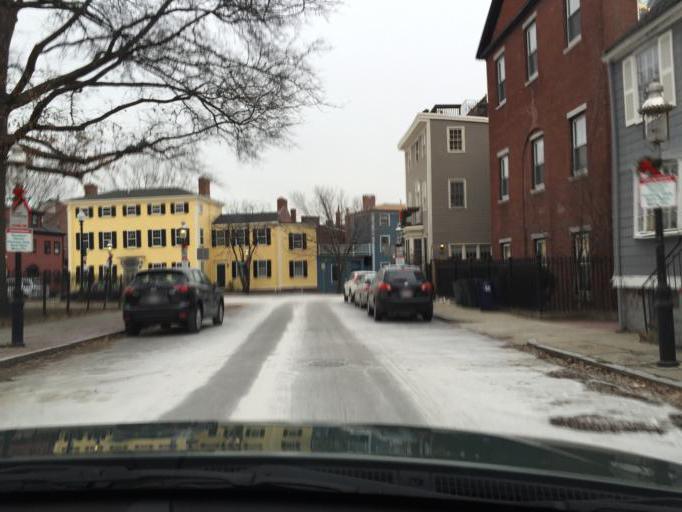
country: US
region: Massachusetts
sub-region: Suffolk County
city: Boston
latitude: 42.3743
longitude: -71.0607
